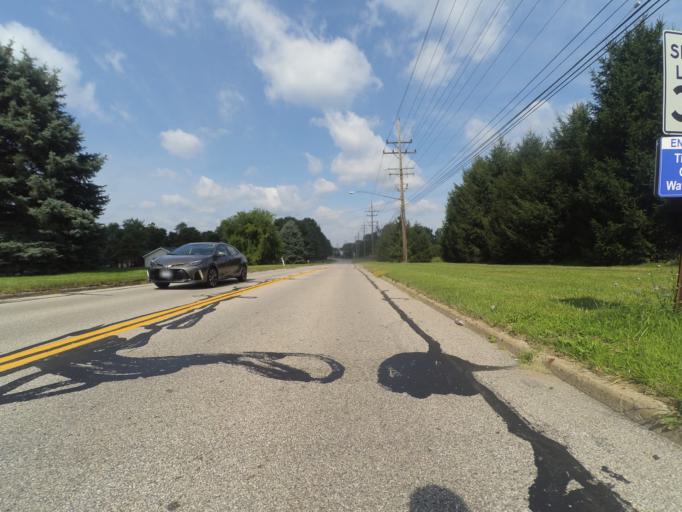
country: US
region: Ohio
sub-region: Cuyahoga County
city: Walton Hills
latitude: 41.3584
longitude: -81.5859
